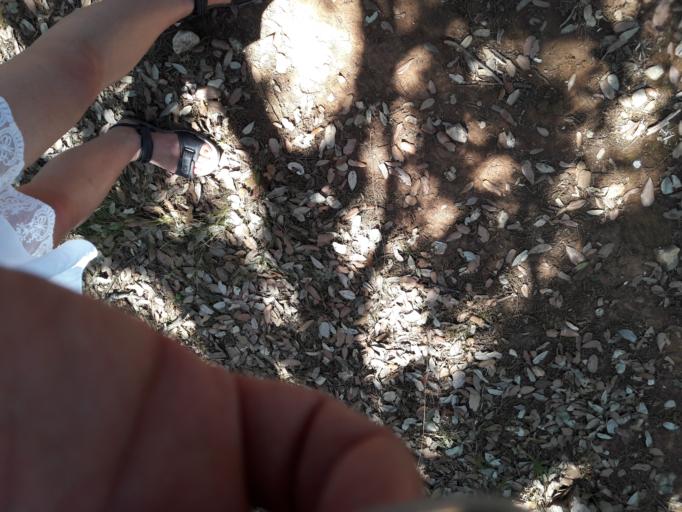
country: HR
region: Licko-Senjska
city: Novalja
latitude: 44.3669
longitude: 14.6988
